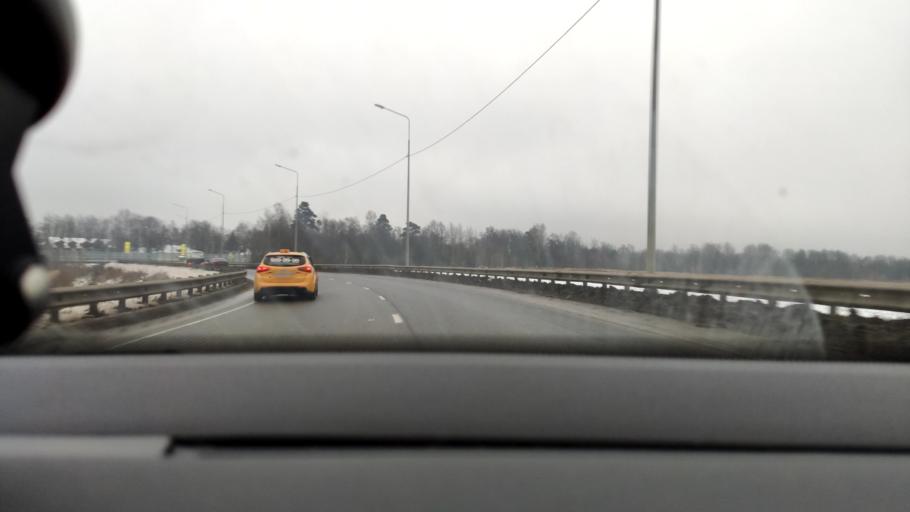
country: RU
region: Moskovskaya
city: Sergiyev Posad
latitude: 56.2723
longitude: 38.1171
